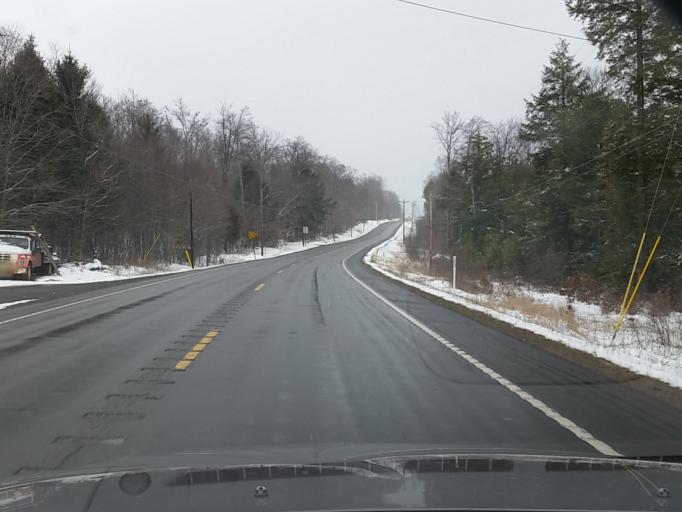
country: US
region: Pennsylvania
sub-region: Sullivan County
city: Laporte
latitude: 41.3932
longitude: -76.5015
